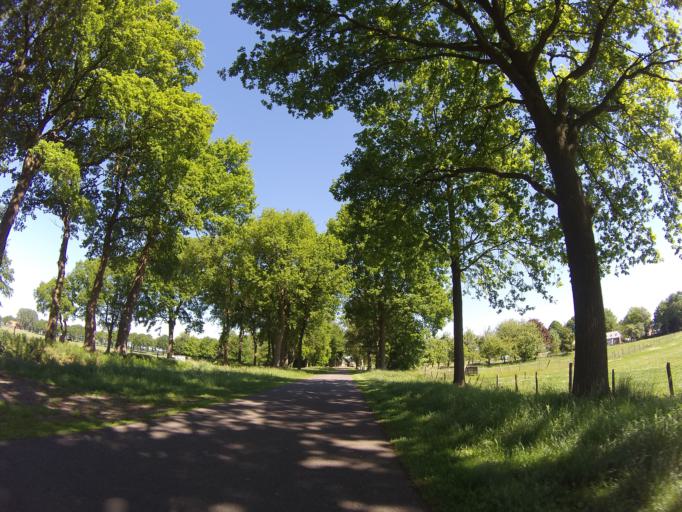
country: NL
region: Drenthe
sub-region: Gemeente Coevorden
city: Sleen
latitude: 52.7779
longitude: 6.7949
